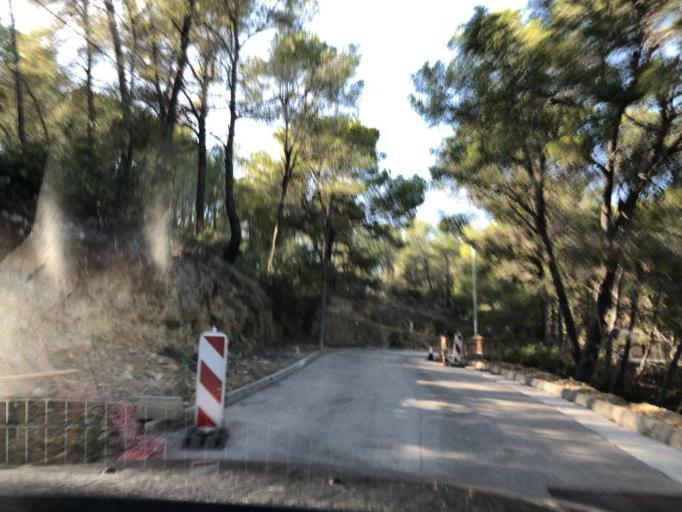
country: ES
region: Balearic Islands
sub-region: Illes Balears
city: Camp de Mar
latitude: 39.5388
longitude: 2.4084
